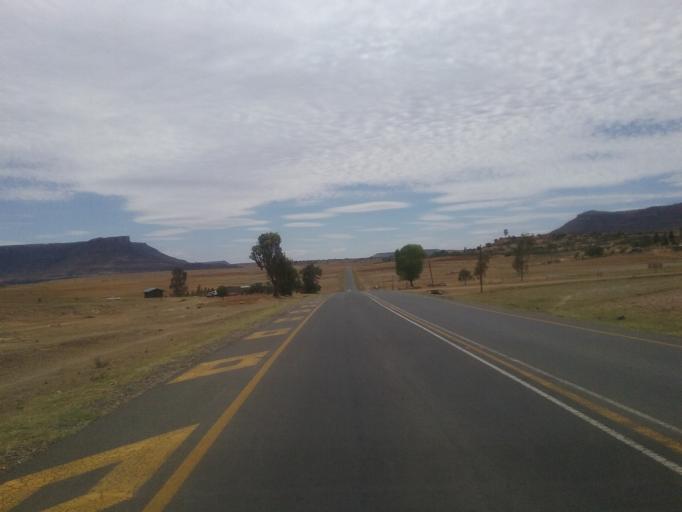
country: LS
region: Mafeteng
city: Mafeteng
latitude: -29.6789
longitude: 27.4459
